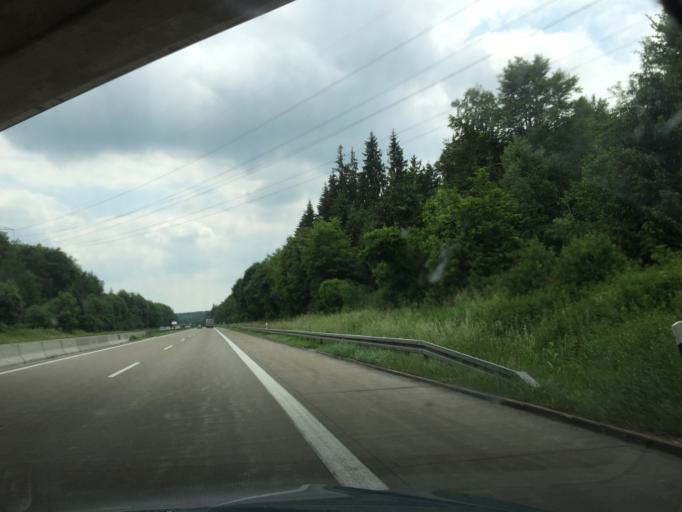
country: DE
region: Baden-Wuerttemberg
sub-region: Regierungsbezirk Stuttgart
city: Nattheim
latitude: 48.7599
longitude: 10.2040
